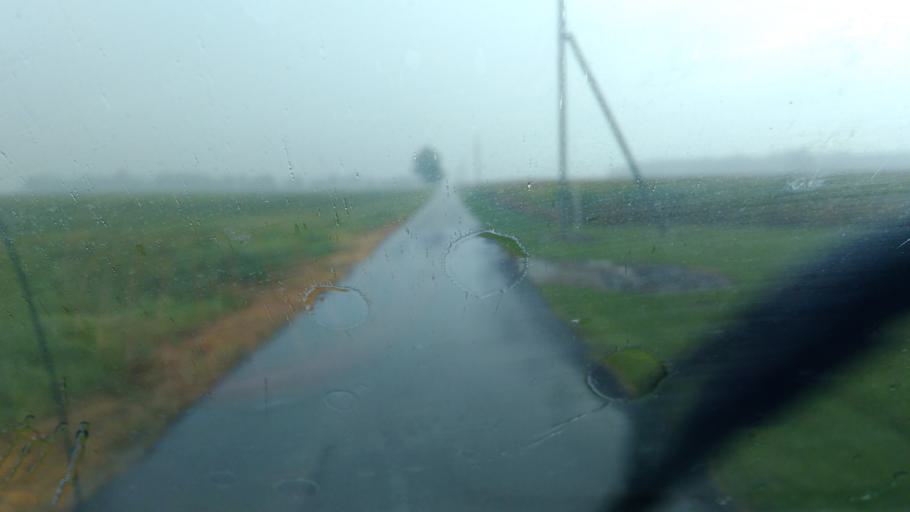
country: US
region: Ohio
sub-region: Hardin County
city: Forest
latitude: 40.7164
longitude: -83.5470
